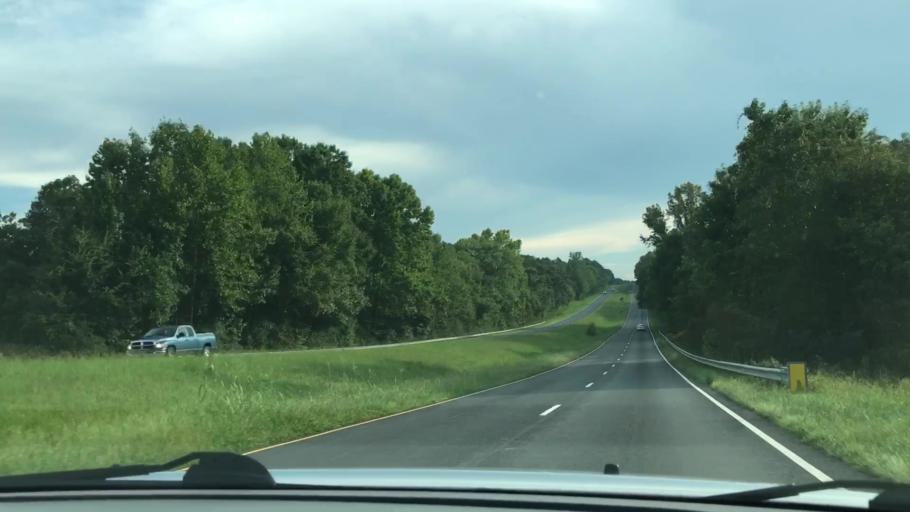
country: US
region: North Carolina
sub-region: Davidson County
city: Denton
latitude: 35.6199
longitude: -80.0108
